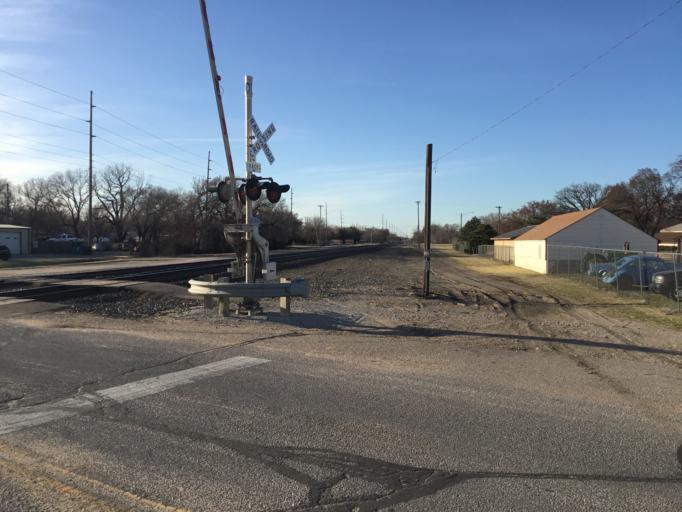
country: US
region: Kansas
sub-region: Sedgwick County
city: Valley Center
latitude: 37.8322
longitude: -97.3754
